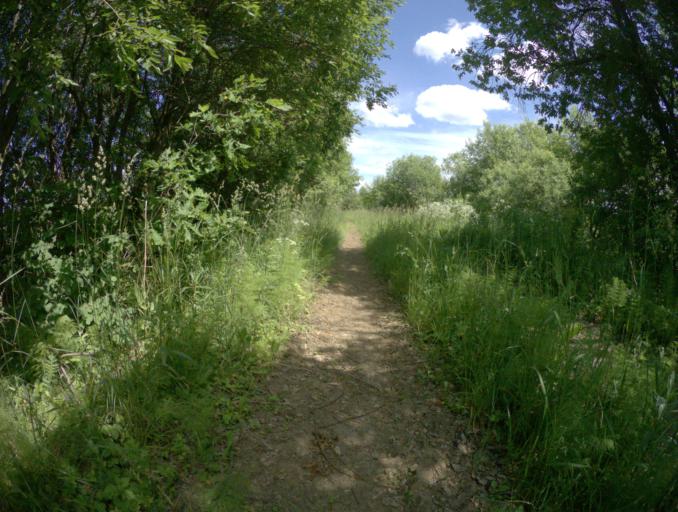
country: RU
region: Ivanovo
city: Gavrilov Posad
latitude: 56.3568
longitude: 40.0533
